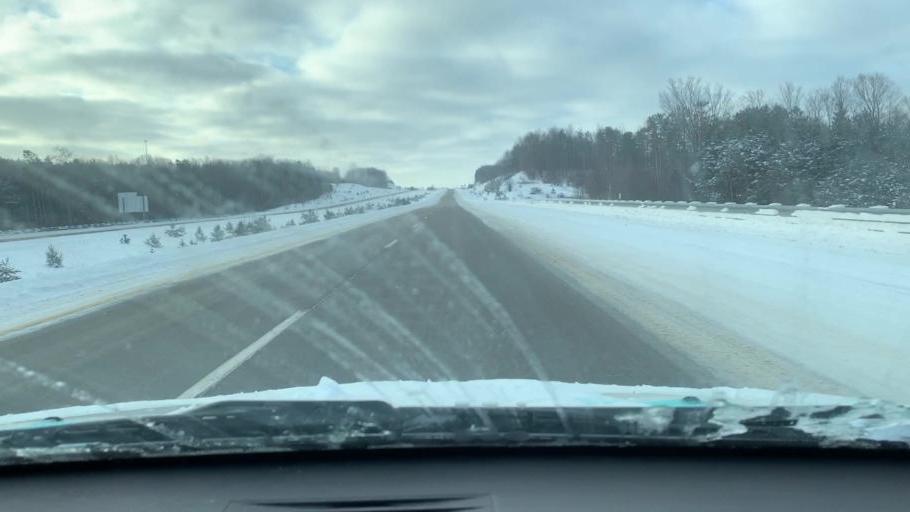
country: US
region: Michigan
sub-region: Wexford County
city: Manton
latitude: 44.4013
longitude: -85.3819
